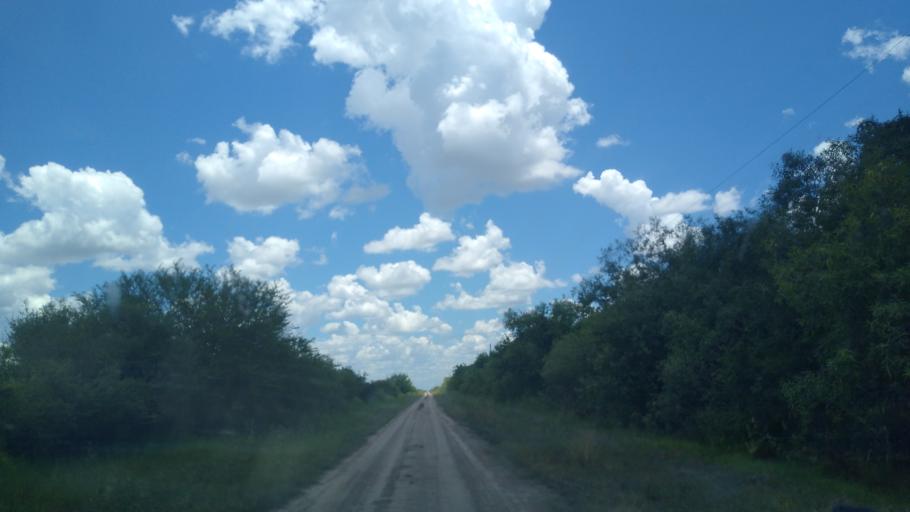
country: AR
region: Chaco
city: Presidencia Roque Saenz Pena
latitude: -26.7472
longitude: -60.3394
